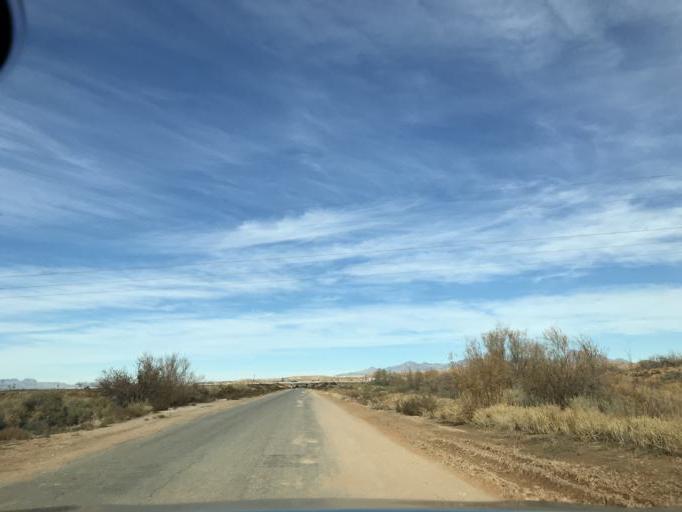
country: US
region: Nevada
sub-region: Clark County
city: Moapa Town
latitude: 36.6606
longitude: -114.5617
